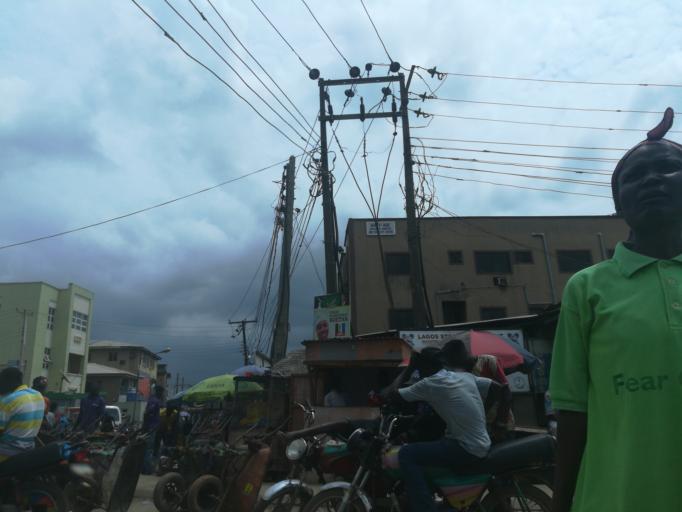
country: NG
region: Lagos
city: Somolu
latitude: 6.5341
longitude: 3.3913
